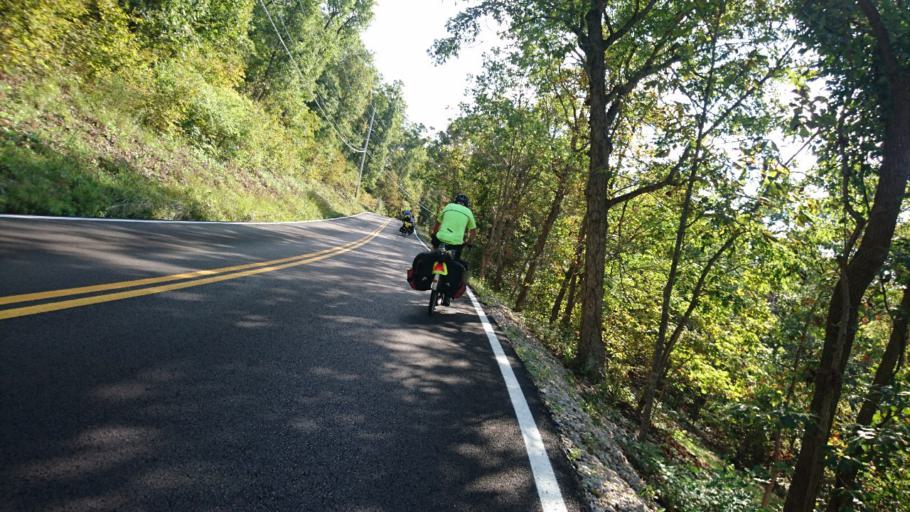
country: US
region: Missouri
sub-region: Saint Louis County
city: Eureka
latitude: 38.5315
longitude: -90.6408
